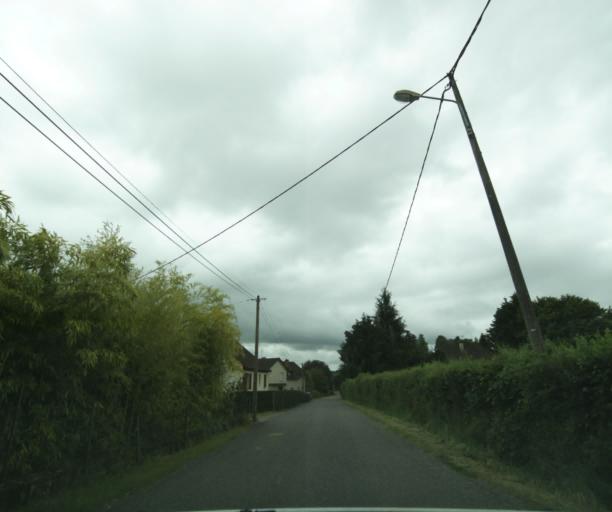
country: FR
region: Bourgogne
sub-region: Departement de Saone-et-Loire
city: Charolles
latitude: 46.4401
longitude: 4.2779
